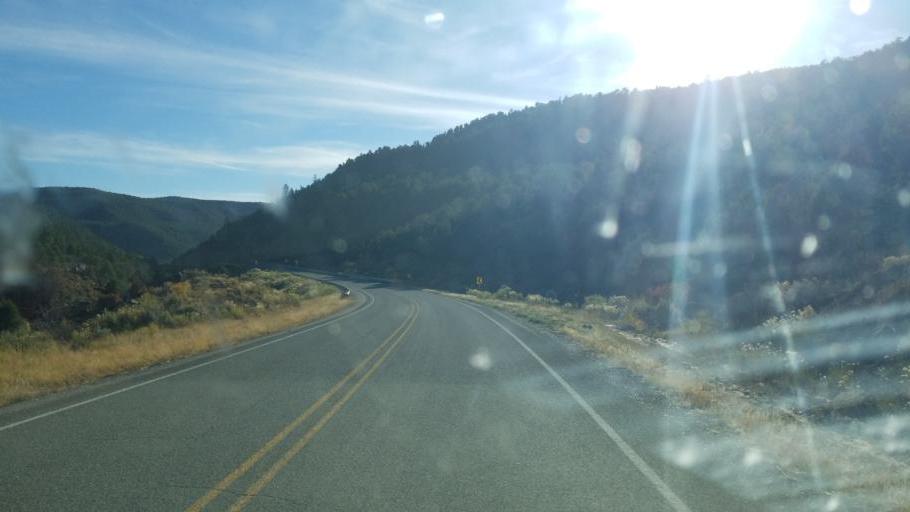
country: US
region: New Mexico
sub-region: Rio Arriba County
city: Navajo
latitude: 36.7297
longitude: -107.2786
